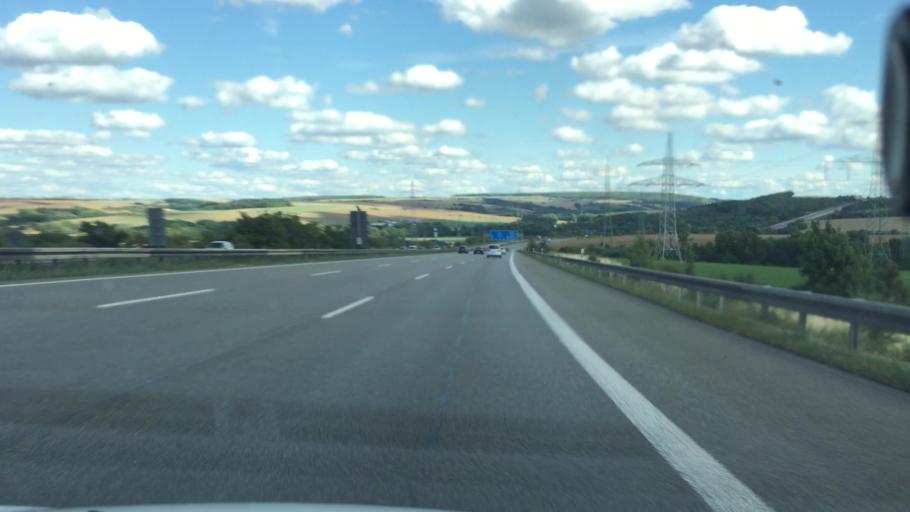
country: DE
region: Thuringia
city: Oettern
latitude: 50.9372
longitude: 11.3718
